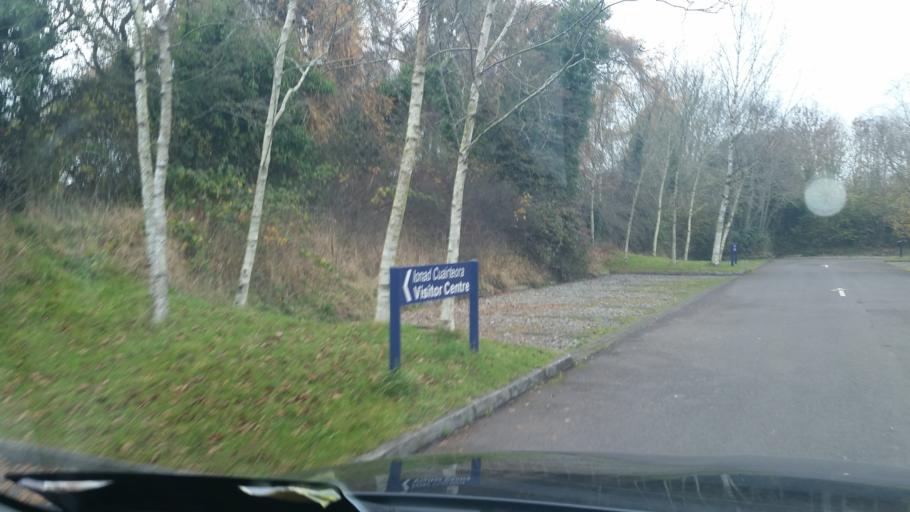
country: IE
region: Leinster
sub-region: An Mhi
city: Duleek
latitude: 53.6951
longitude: -6.4473
